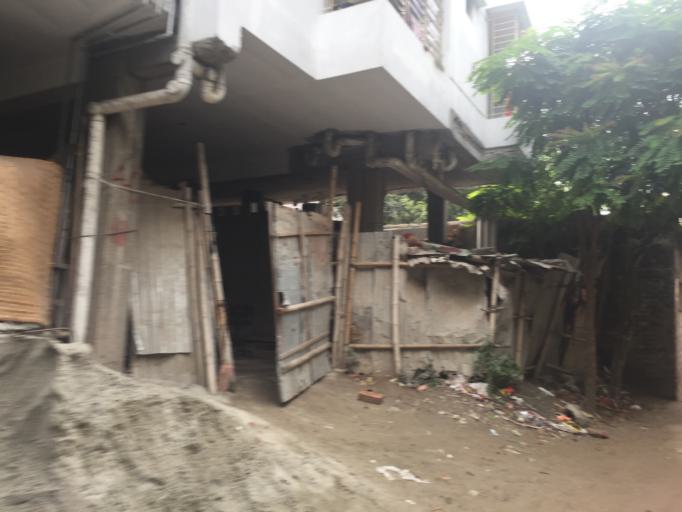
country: BD
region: Dhaka
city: Azimpur
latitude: 23.7841
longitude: 90.3642
